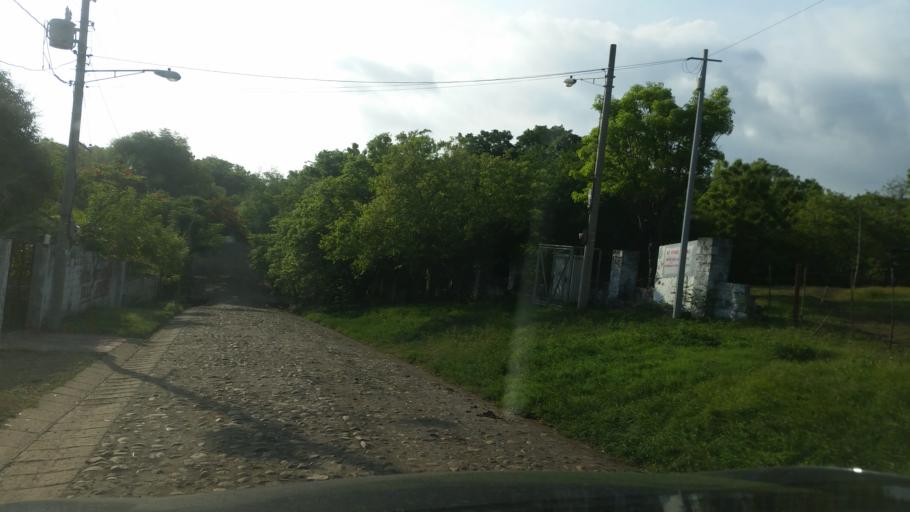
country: NI
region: Managua
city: Masachapa
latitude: 11.7576
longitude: -86.4898
